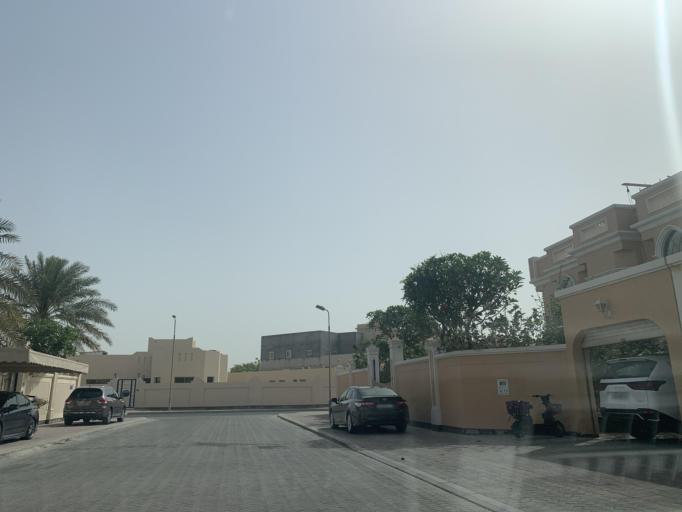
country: BH
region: Central Governorate
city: Madinat Hamad
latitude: 26.1410
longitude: 50.5130
